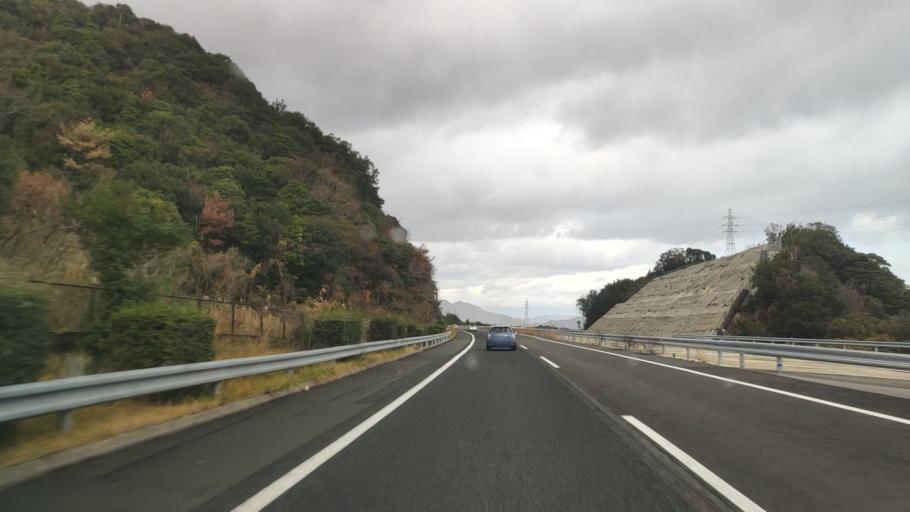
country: JP
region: Tokushima
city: Ishii
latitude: 34.2009
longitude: 134.4293
